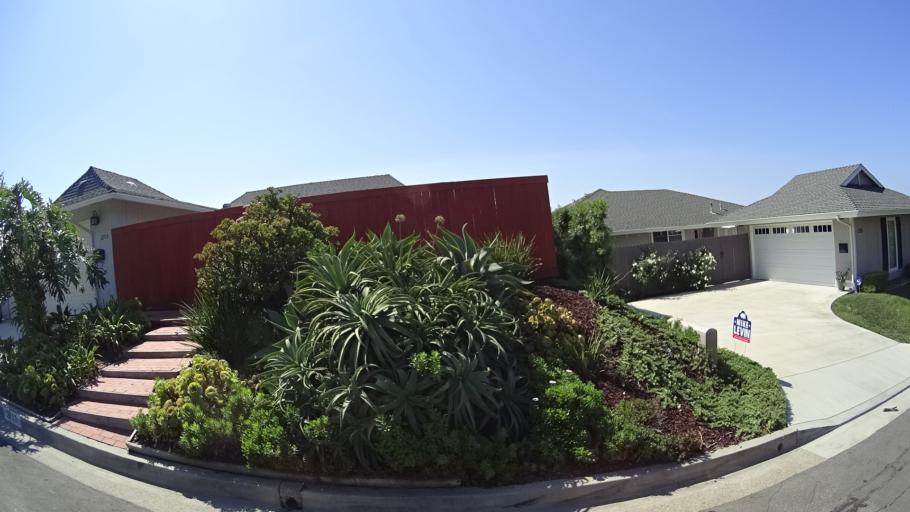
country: US
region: California
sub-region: Orange County
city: San Clemente
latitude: 33.4451
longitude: -117.6405
